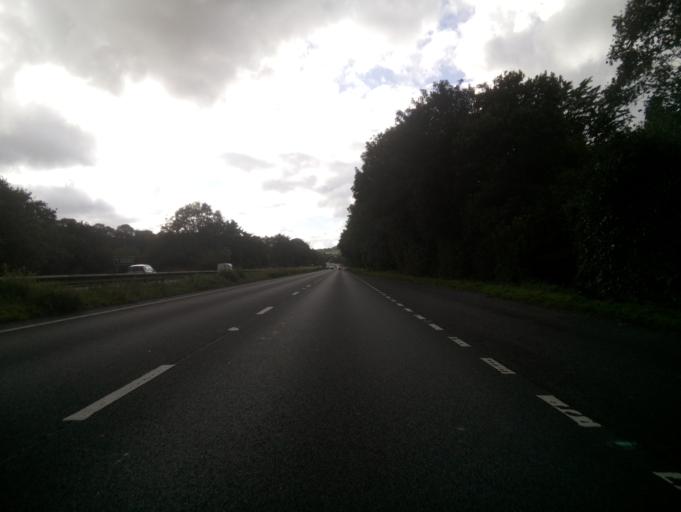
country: GB
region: England
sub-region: Devon
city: Ivybridge
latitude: 50.3850
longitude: -3.9204
